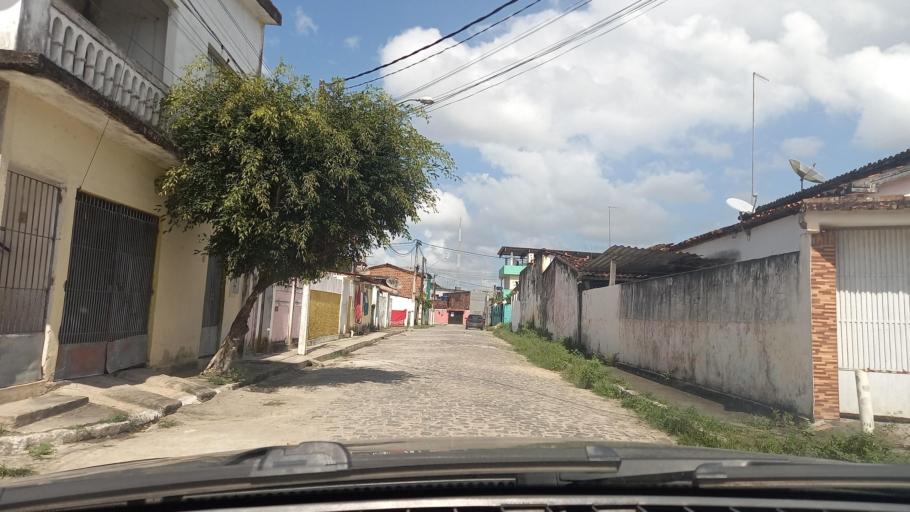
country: BR
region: Pernambuco
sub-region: Goiana
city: Goiana
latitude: -7.5615
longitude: -34.9950
